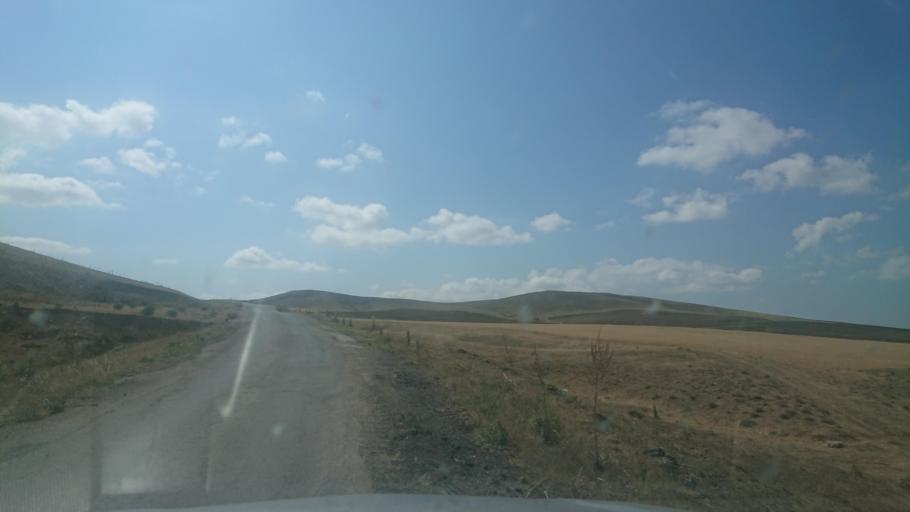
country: TR
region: Aksaray
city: Sariyahsi
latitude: 39.0079
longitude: 33.9501
